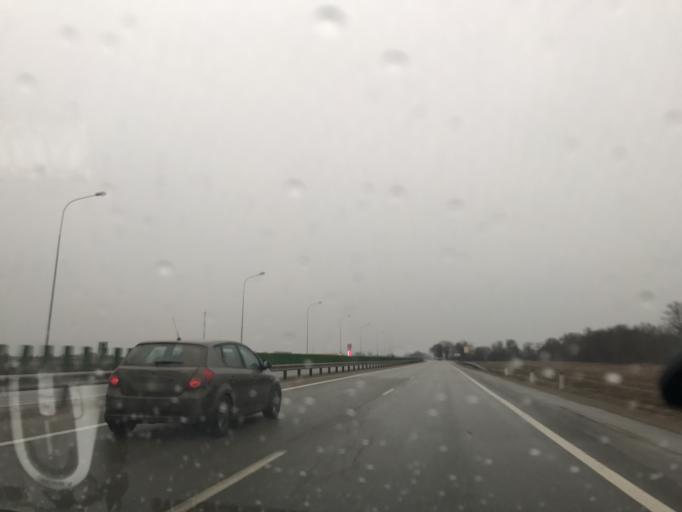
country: RU
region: Krasnodarskiy
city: Pavlovskaya
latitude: 46.2739
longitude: 39.8317
